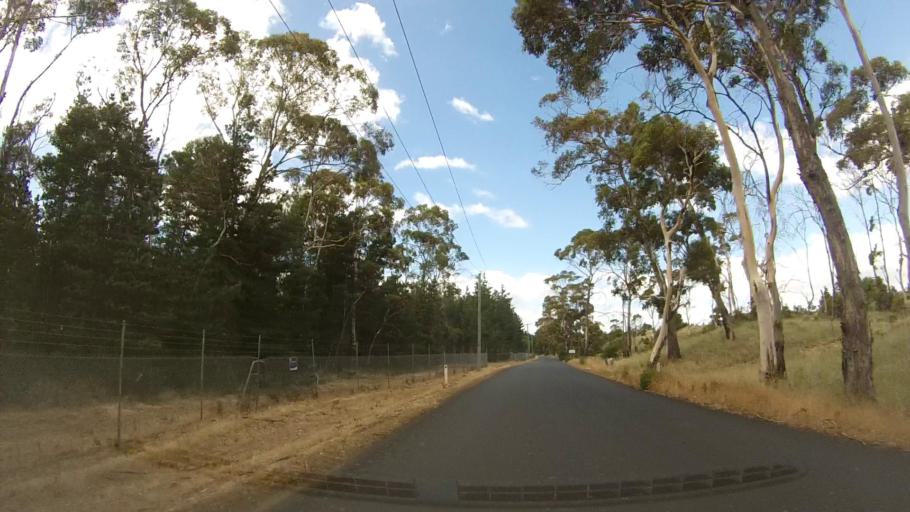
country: AU
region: Tasmania
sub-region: Clarence
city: Seven Mile Beach
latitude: -42.8444
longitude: 147.5305
